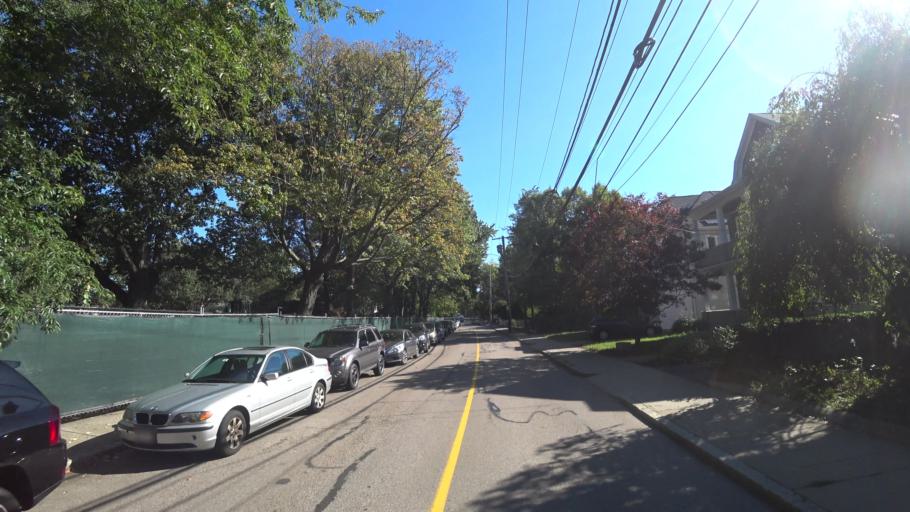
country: US
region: Massachusetts
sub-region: Norfolk County
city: Brookline
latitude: 42.3319
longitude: -71.1227
